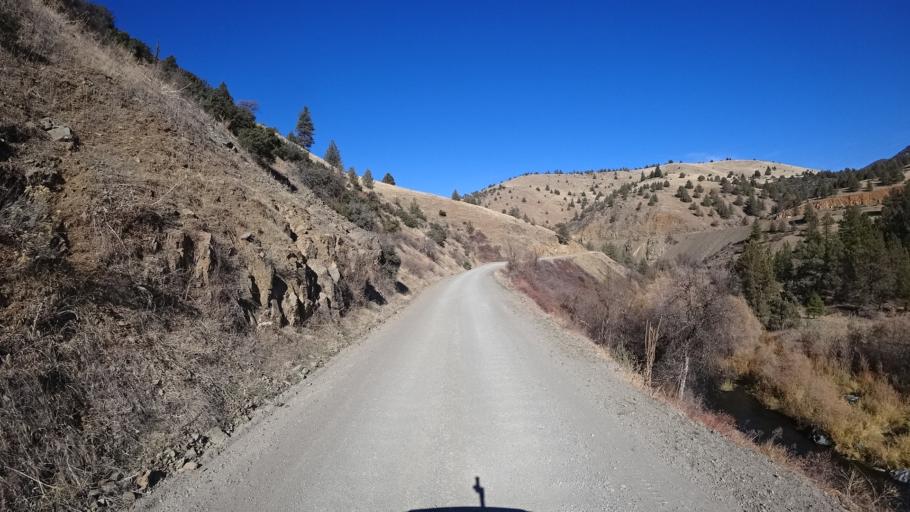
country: US
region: California
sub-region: Siskiyou County
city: Yreka
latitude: 41.7841
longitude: -122.6040
